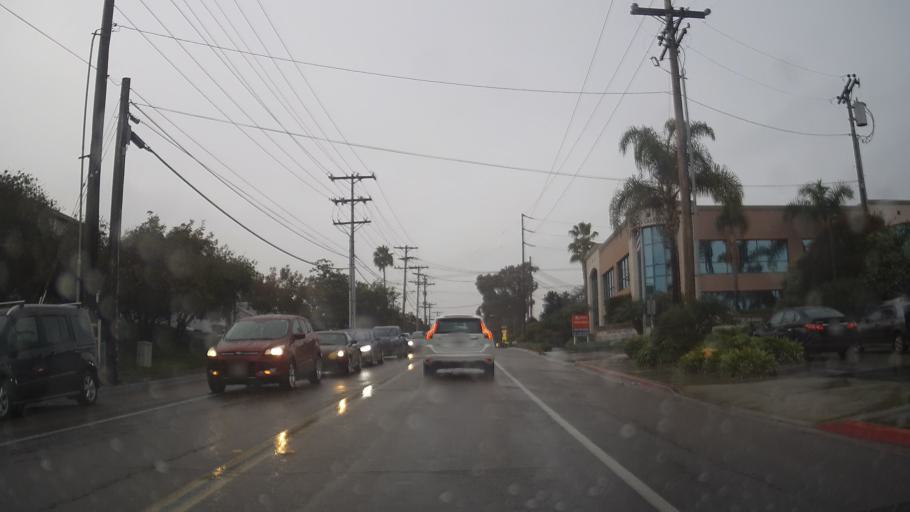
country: US
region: California
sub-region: San Diego County
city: Encinitas
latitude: 33.0495
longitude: -117.2857
